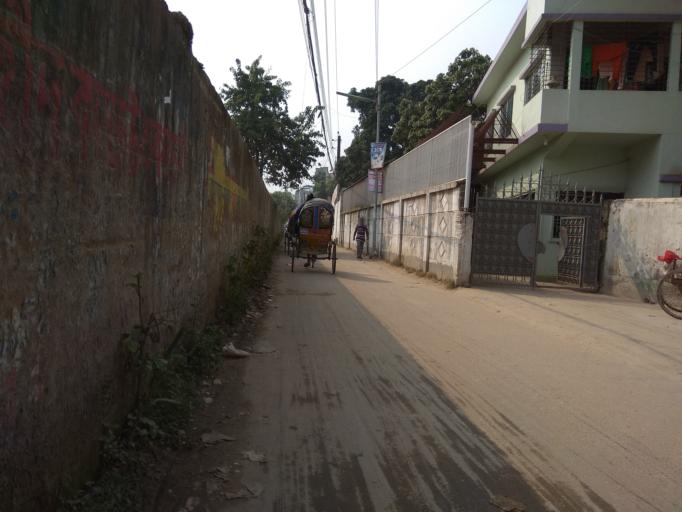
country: BD
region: Dhaka
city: Tungi
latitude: 23.8614
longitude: 90.3925
